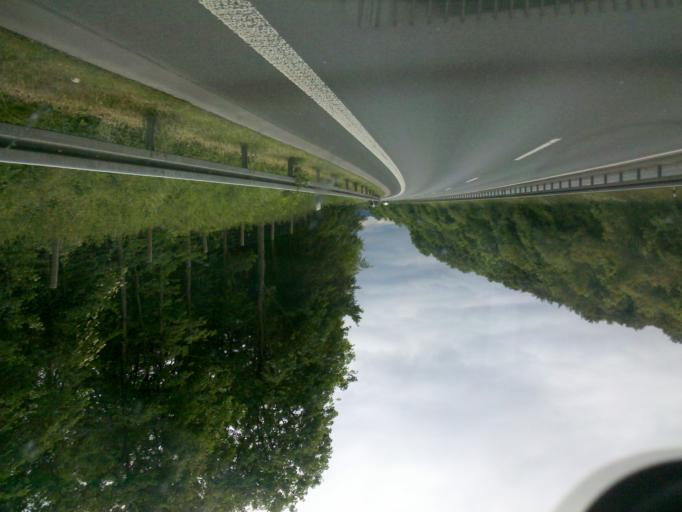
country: DE
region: North Rhine-Westphalia
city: Kreuztal
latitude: 50.9446
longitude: 8.0047
